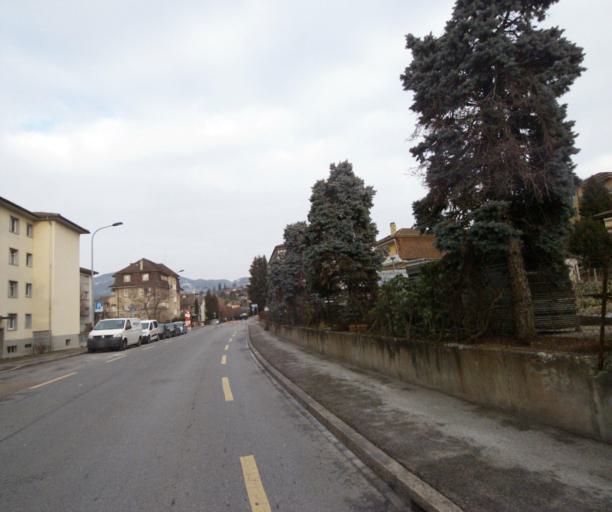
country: CH
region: Vaud
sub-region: Riviera-Pays-d'Enhaut District
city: La Tour-de-Peilz
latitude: 46.4581
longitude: 6.8622
